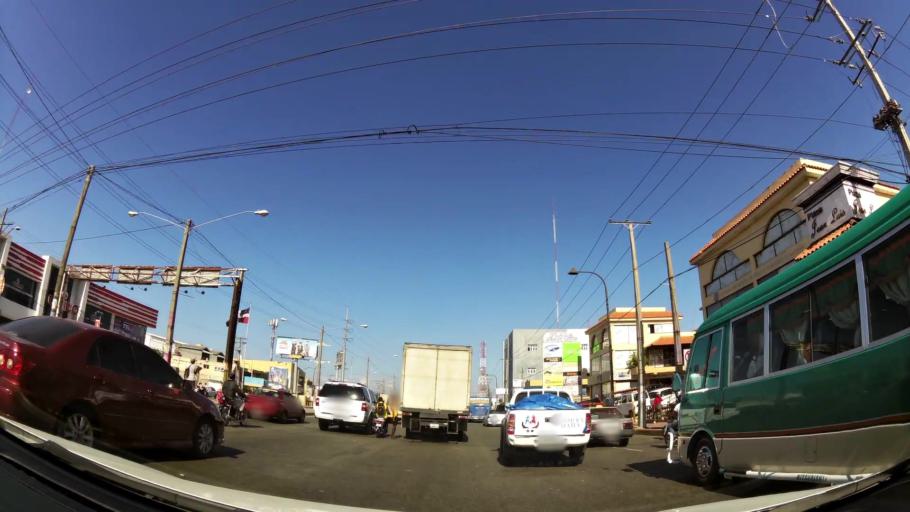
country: DO
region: Nacional
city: Bella Vista
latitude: 18.4509
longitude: -69.9781
